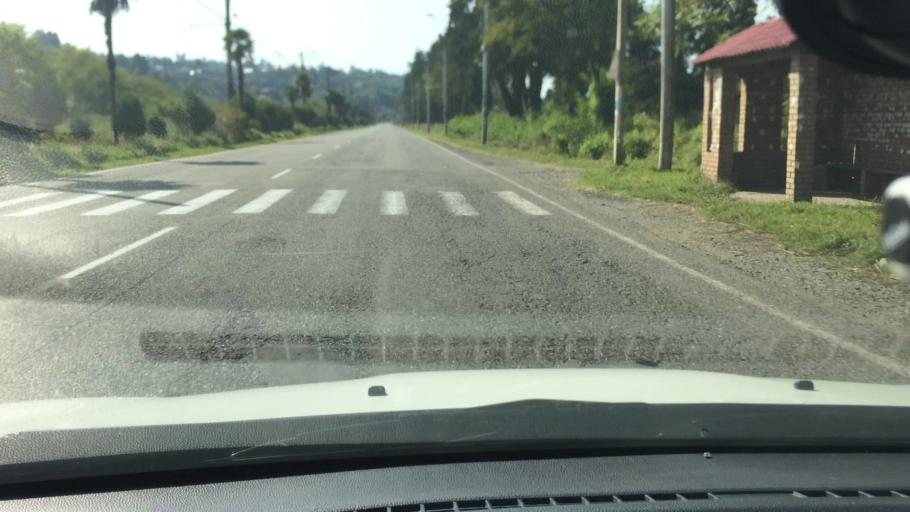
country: GE
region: Ajaria
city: Kobuleti
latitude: 41.7866
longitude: 41.7663
